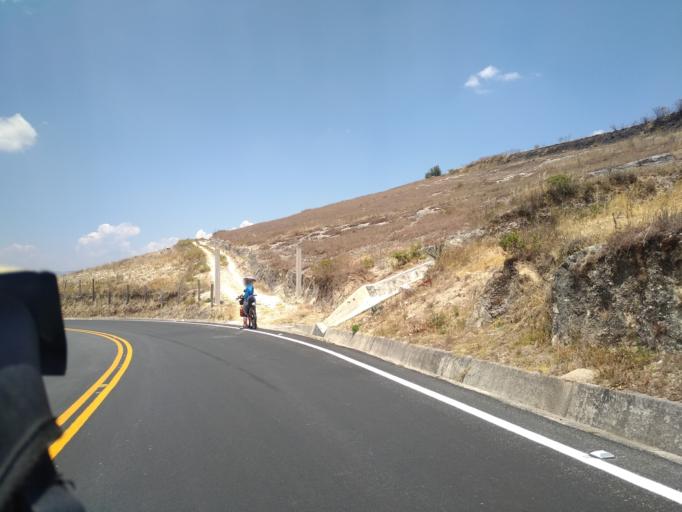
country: PE
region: Cajamarca
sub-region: San Marcos
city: San Marcos
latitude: -7.2753
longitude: -78.2466
